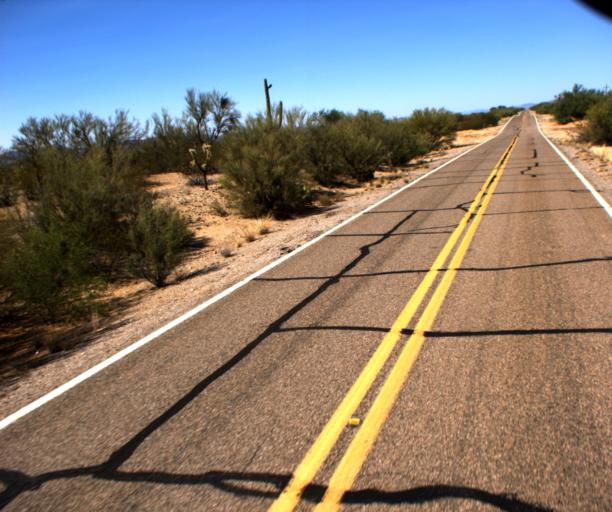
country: US
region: Arizona
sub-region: Pima County
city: Three Points
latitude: 31.9844
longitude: -111.3728
